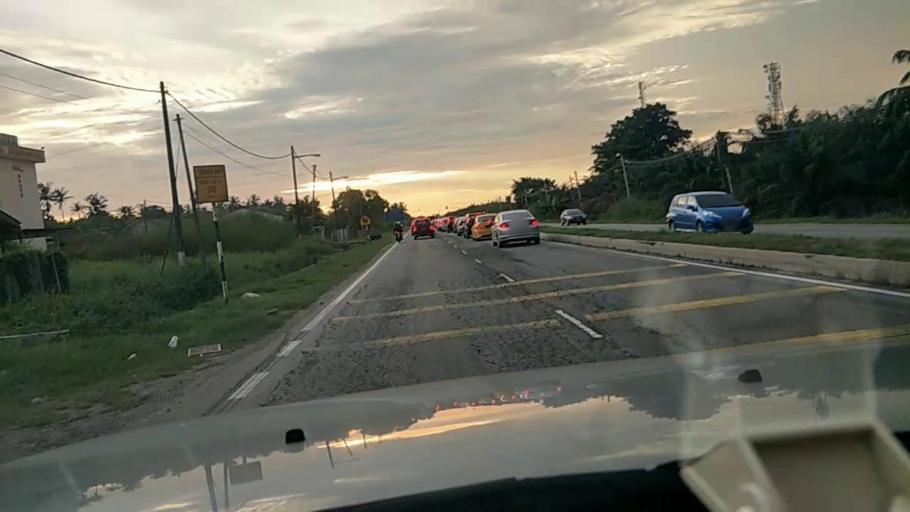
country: MY
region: Perak
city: Kampong Dungun
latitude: 3.1454
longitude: 101.3518
